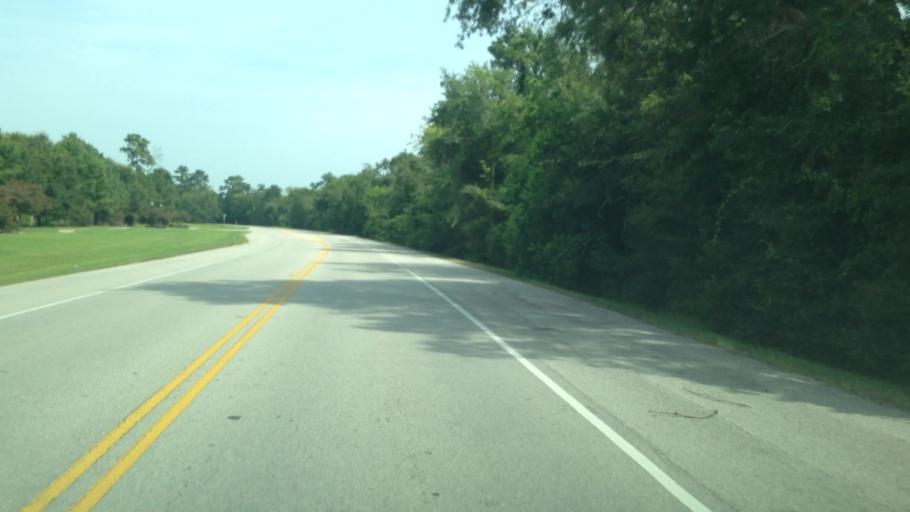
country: US
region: Texas
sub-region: Harris County
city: Atascocita
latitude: 29.9286
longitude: -95.1740
